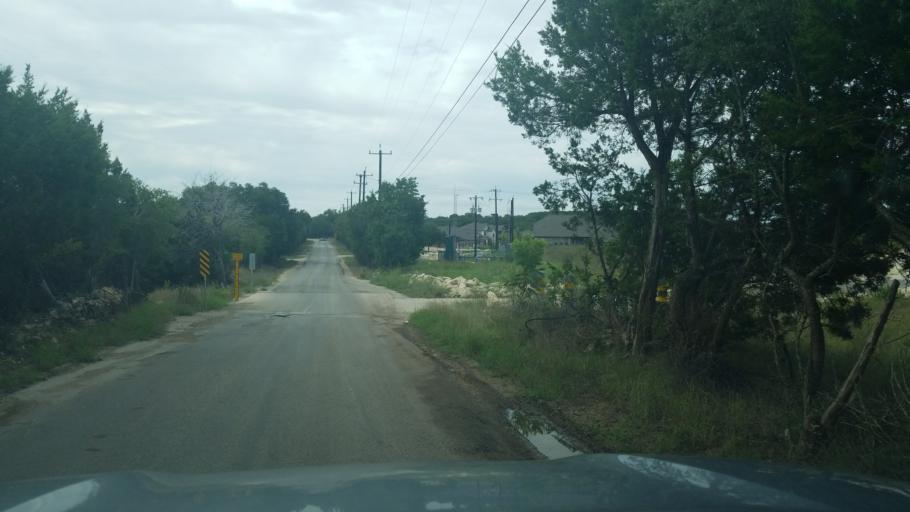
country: US
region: Texas
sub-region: Comal County
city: Bulverde
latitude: 29.7706
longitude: -98.4138
